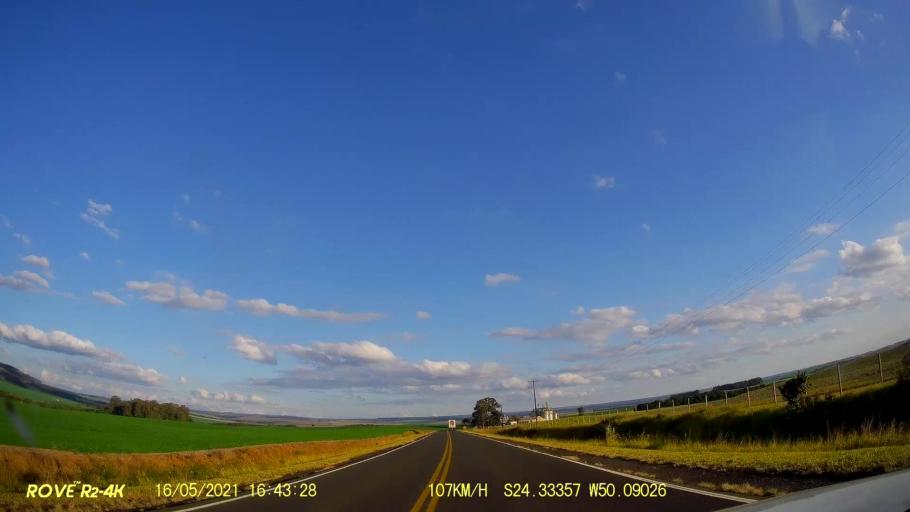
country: BR
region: Parana
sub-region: Pirai Do Sul
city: Pirai do Sul
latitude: -24.3340
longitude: -50.0900
